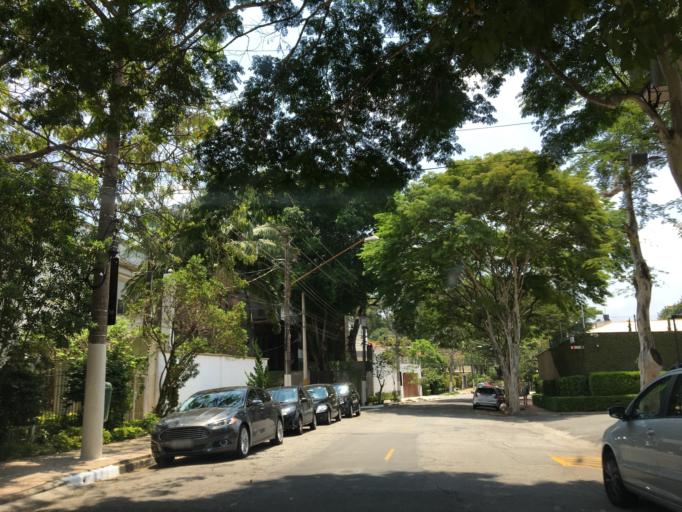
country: BR
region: Sao Paulo
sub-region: Sao Paulo
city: Sao Paulo
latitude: -23.5916
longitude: -46.6537
